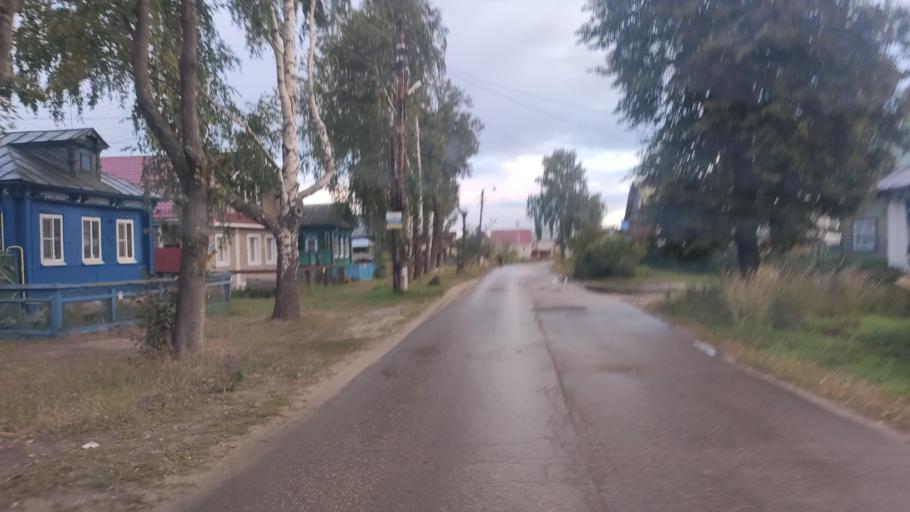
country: RU
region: Nizjnij Novgorod
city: Taremskoye
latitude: 55.9928
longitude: 43.0128
